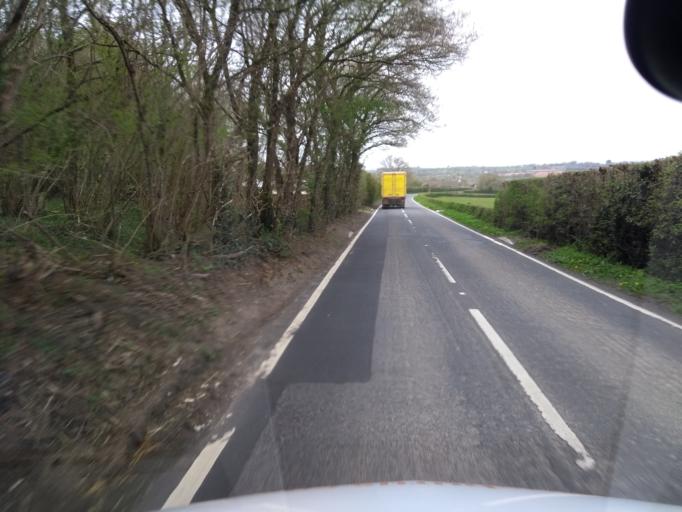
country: GB
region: England
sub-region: Somerset
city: Curry Rivel
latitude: 51.0047
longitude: -2.9509
